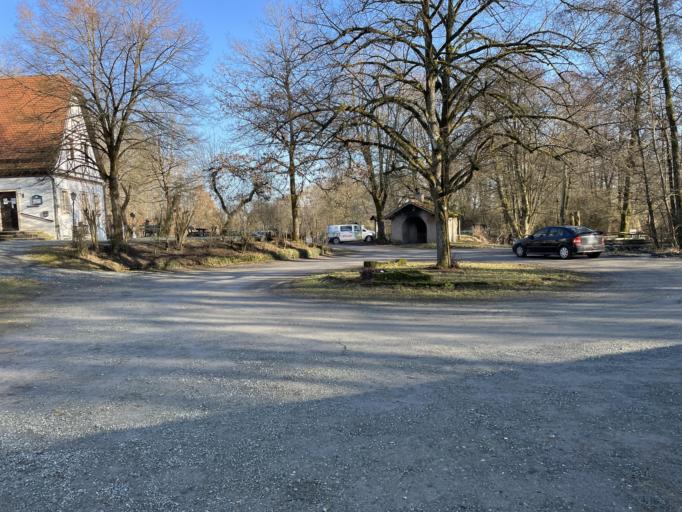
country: DE
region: Bavaria
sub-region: Upper Franconia
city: Speichersdorf
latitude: 49.8888
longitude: 11.8001
